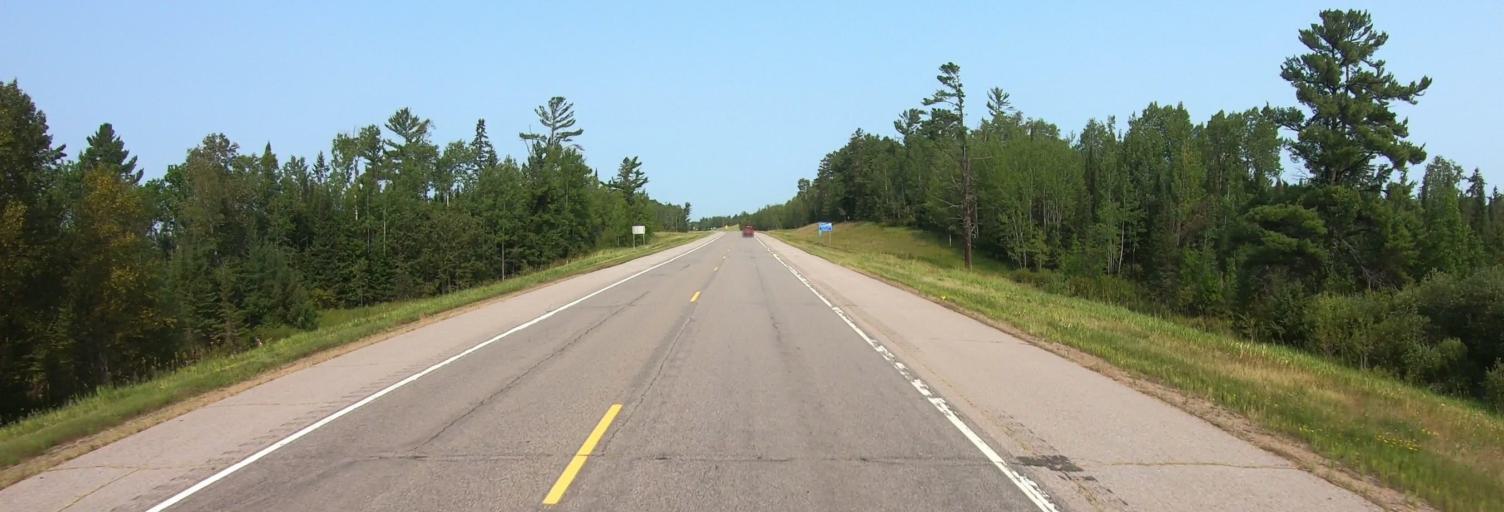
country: US
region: Minnesota
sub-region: Saint Louis County
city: Mountain Iron
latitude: 47.8852
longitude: -92.7674
